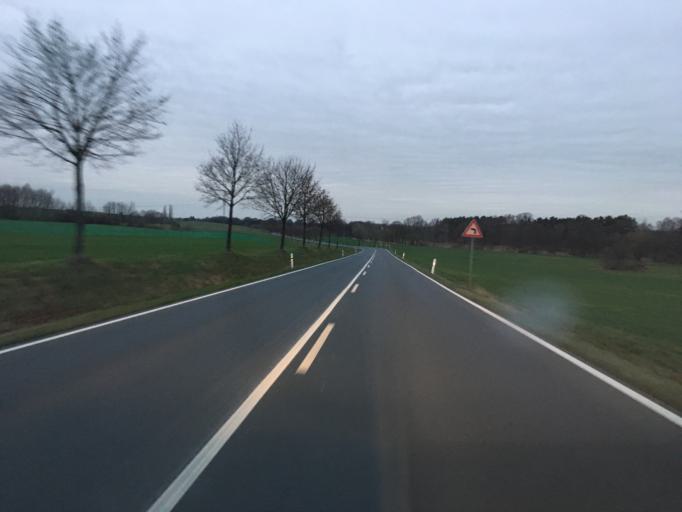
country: DE
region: Saxony
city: Dahlen
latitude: 51.3250
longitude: 13.0359
